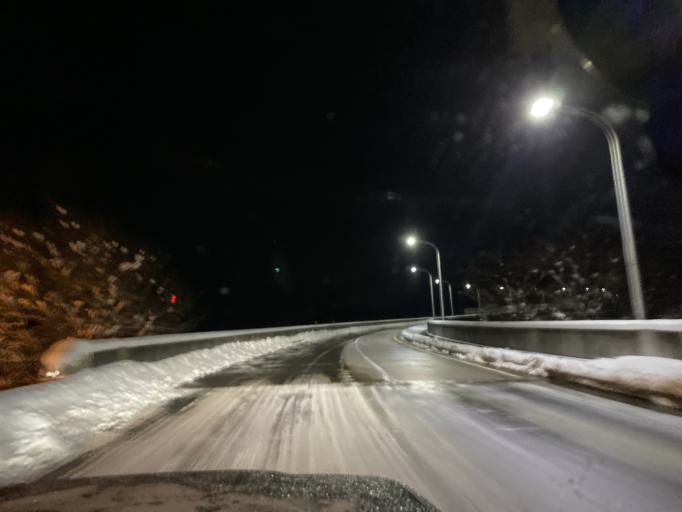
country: JP
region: Nagano
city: Omachi
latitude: 36.5405
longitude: 137.8425
